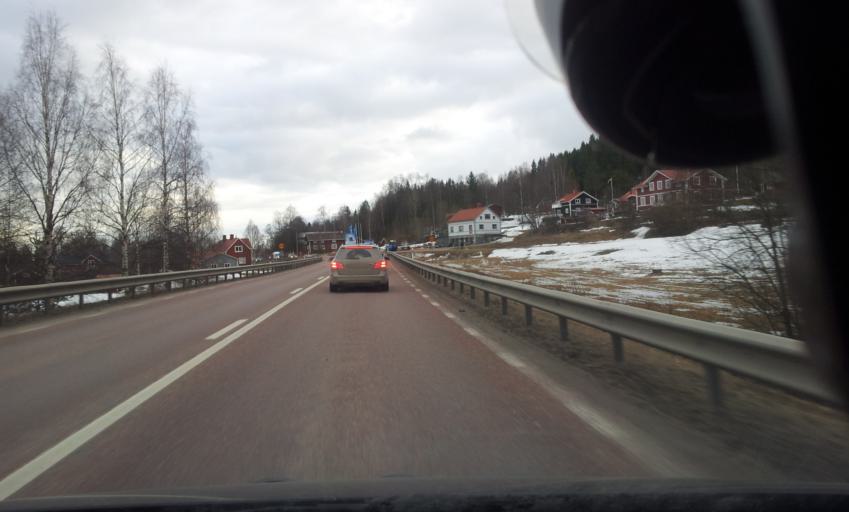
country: SE
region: Gaevleborg
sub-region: Ljusdals Kommun
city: Jaervsoe
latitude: 61.7238
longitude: 16.1685
